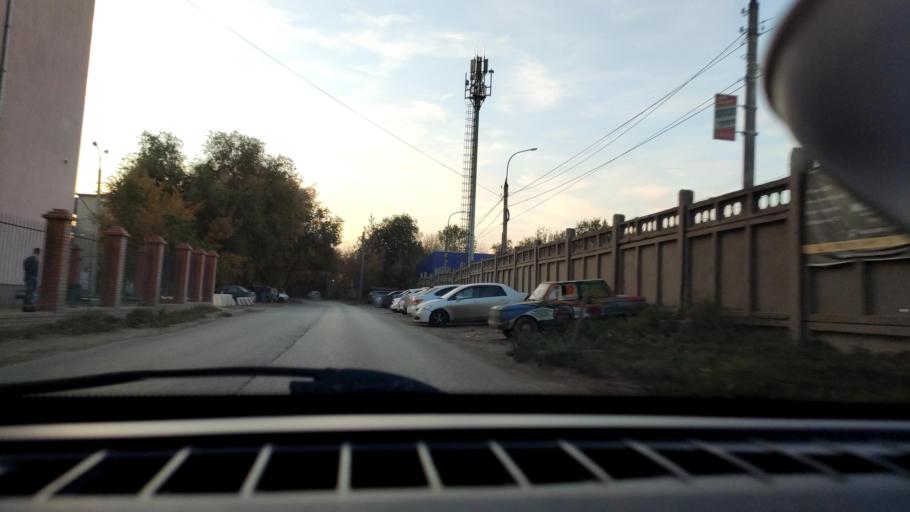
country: RU
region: Samara
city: Samara
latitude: 53.2021
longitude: 50.2523
